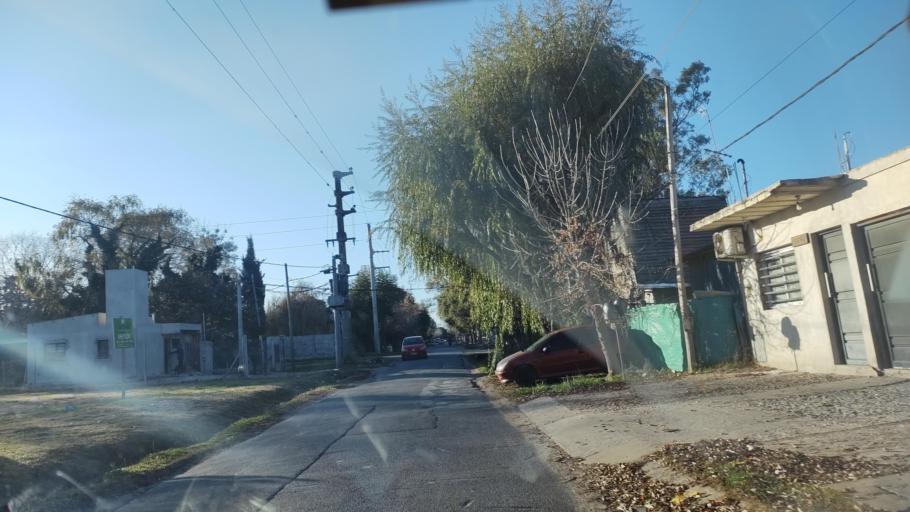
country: AR
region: Buenos Aires
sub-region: Partido de La Plata
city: La Plata
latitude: -34.8852
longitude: -58.0685
